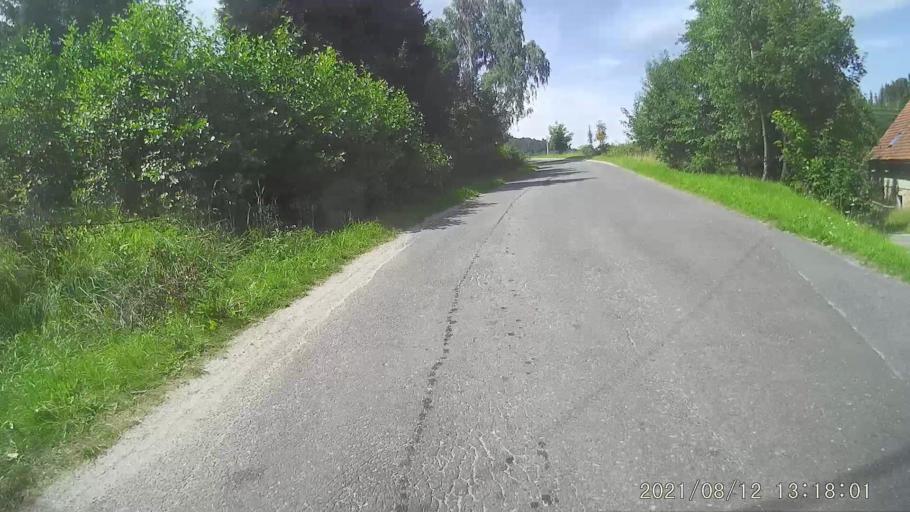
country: PL
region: Lower Silesian Voivodeship
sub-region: Powiat klodzki
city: Stronie Slaskie
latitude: 50.2717
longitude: 16.8881
